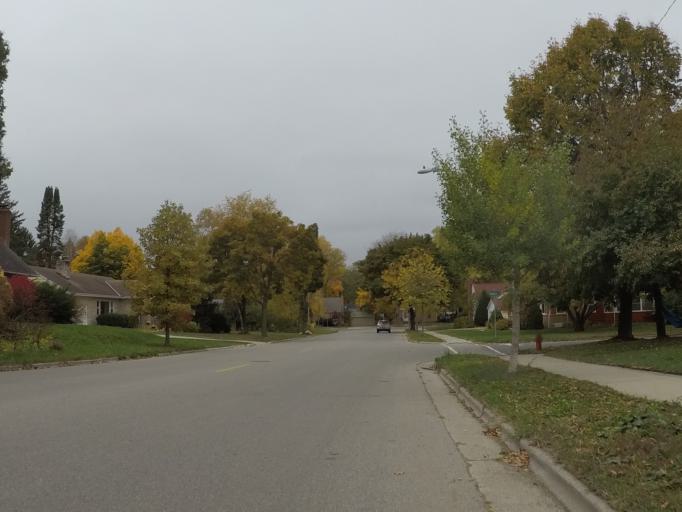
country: US
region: Wisconsin
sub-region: Dane County
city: Shorewood Hills
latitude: 43.0695
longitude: -89.4448
